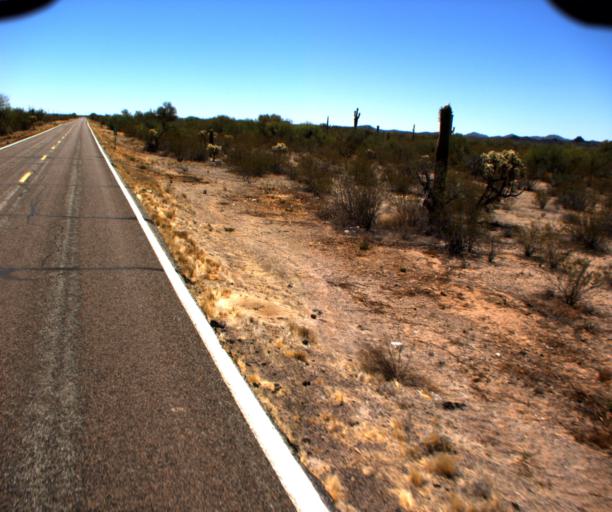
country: US
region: Arizona
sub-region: Pima County
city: Ajo
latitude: 32.2213
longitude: -112.6657
